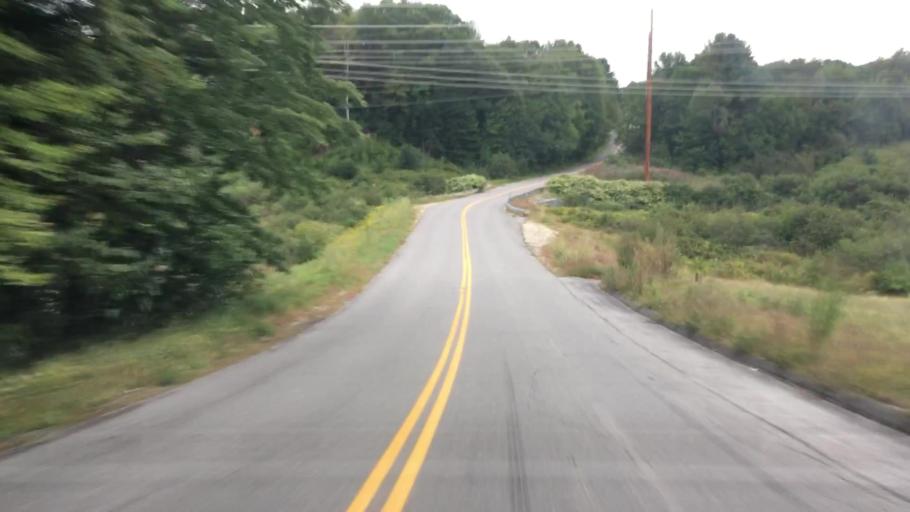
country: US
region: Maine
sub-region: Cumberland County
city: New Gloucester
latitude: 43.9085
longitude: -70.2228
